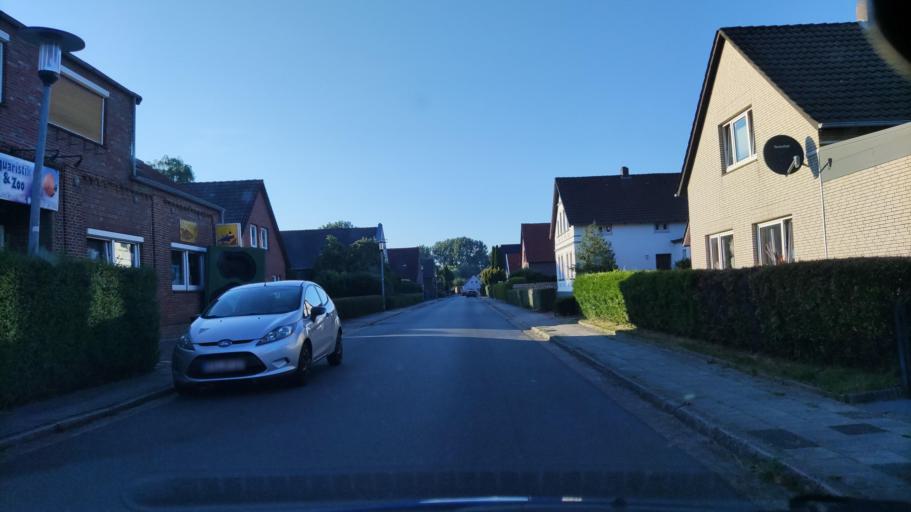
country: DE
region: Lower Saxony
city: Wittmund
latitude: 53.5764
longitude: 7.7900
